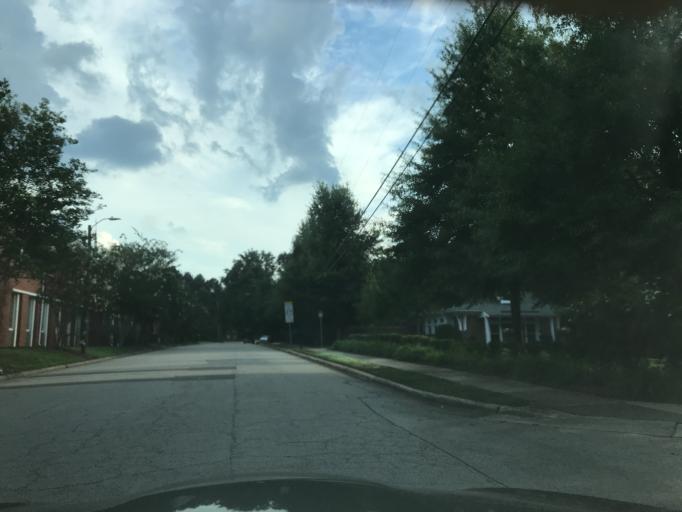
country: US
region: North Carolina
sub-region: Wake County
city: West Raleigh
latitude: 35.8110
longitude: -78.6345
